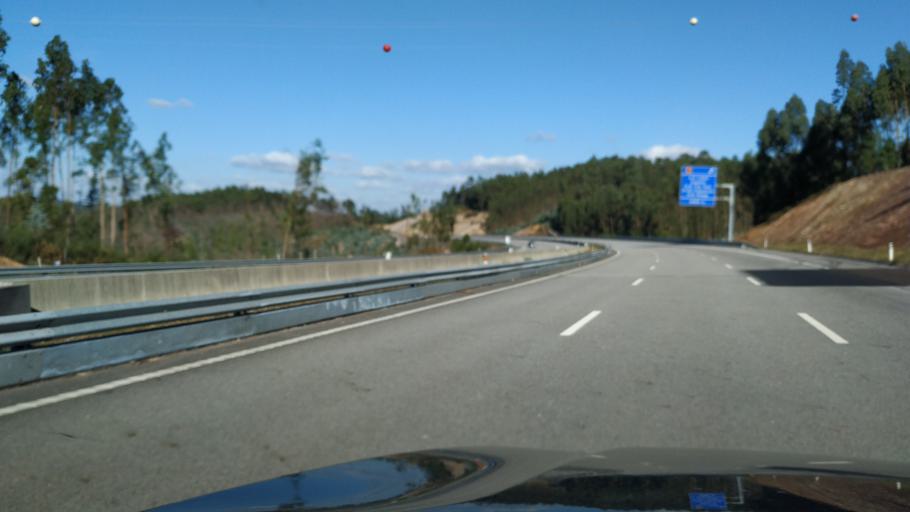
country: PT
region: Porto
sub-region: Vila Nova de Gaia
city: Sandim
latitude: 41.0221
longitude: -8.4784
